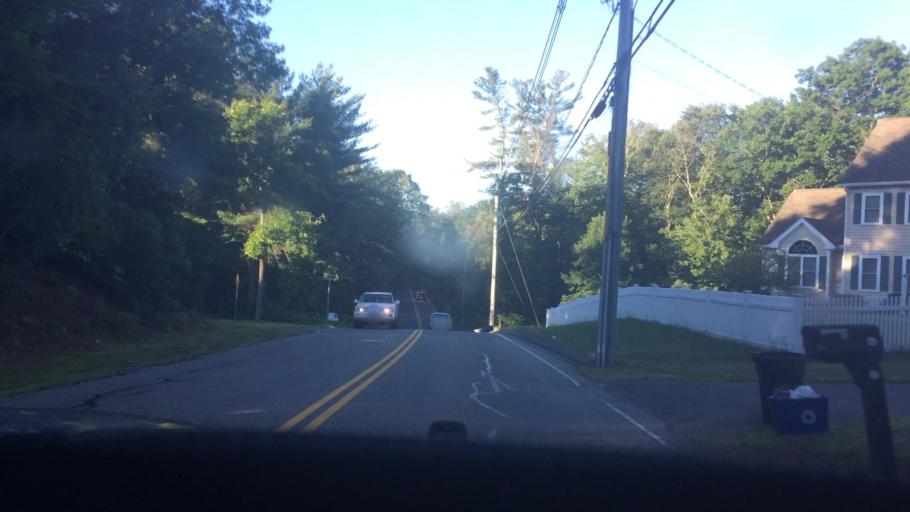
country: US
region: Massachusetts
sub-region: Essex County
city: Andover
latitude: 42.6345
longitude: -71.0904
